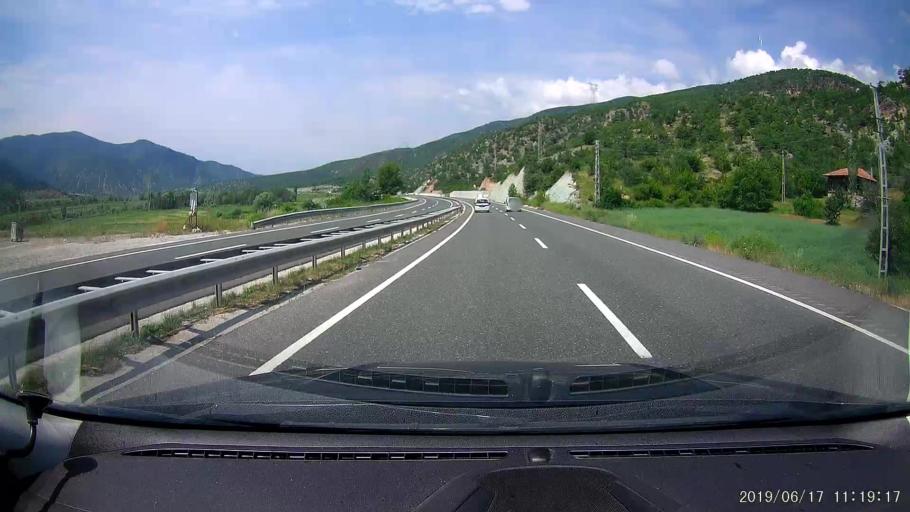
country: TR
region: Cankiri
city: Yaprakli
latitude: 40.9265
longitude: 33.8324
